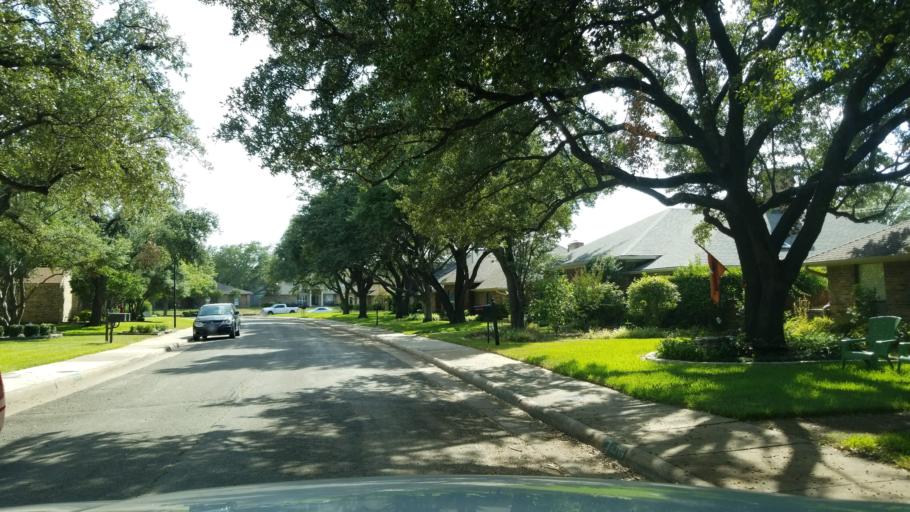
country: US
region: Texas
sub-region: Dallas County
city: Addison
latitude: 32.9683
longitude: -96.7984
